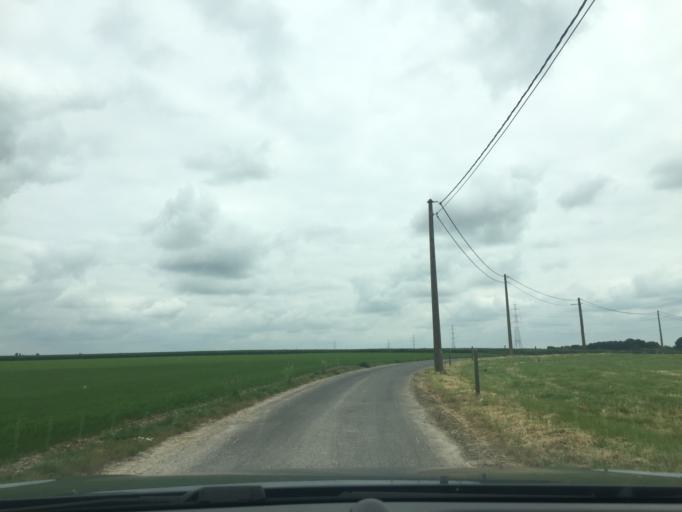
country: FR
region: Nord-Pas-de-Calais
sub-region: Departement du Nord
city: Leers
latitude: 50.6556
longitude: 3.2804
